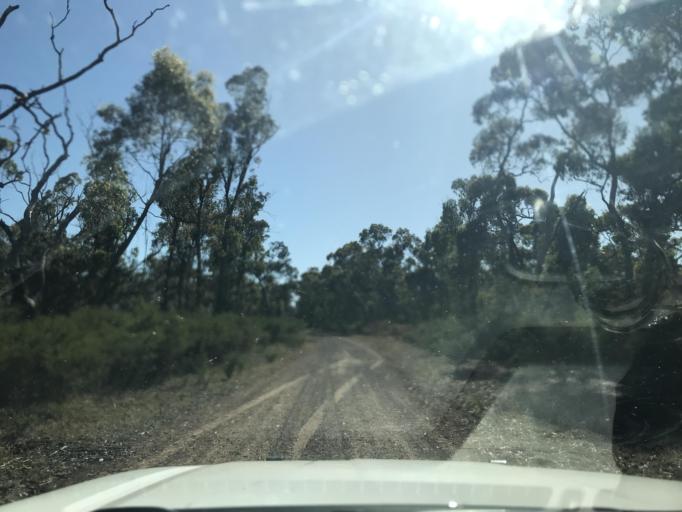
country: AU
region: South Australia
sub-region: Wattle Range
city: Penola
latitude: -37.0726
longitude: 141.4097
